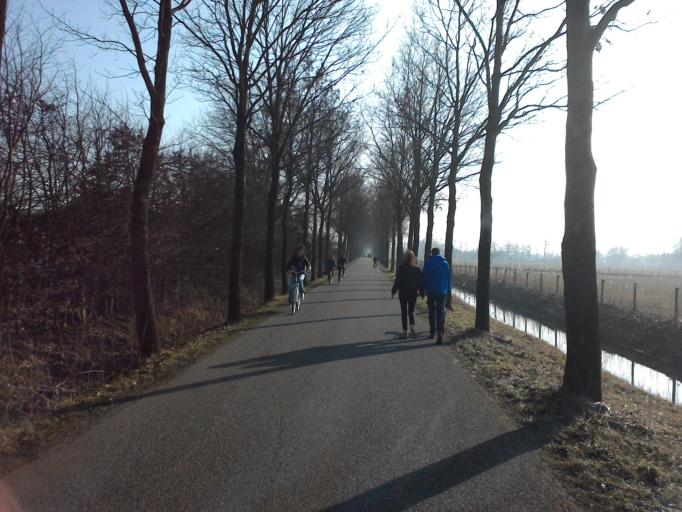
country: NL
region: Utrecht
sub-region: Gemeente Bunnik
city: Bunnik
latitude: 52.0820
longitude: 5.1940
